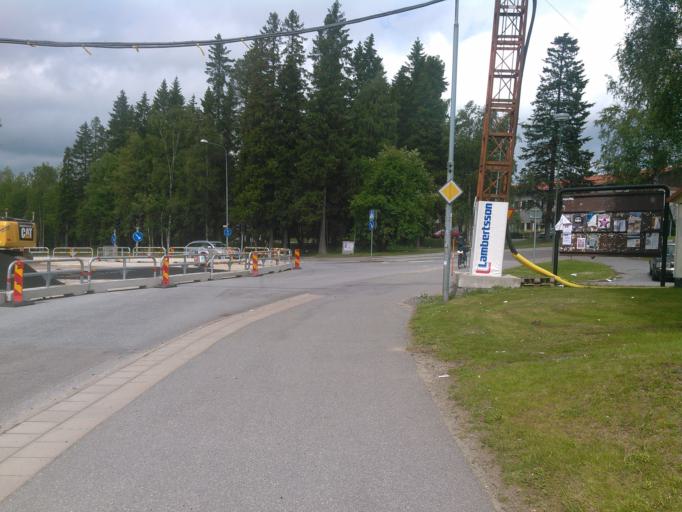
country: SE
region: Vaesterbotten
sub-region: Umea Kommun
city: Umea
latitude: 63.8262
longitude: 20.2944
